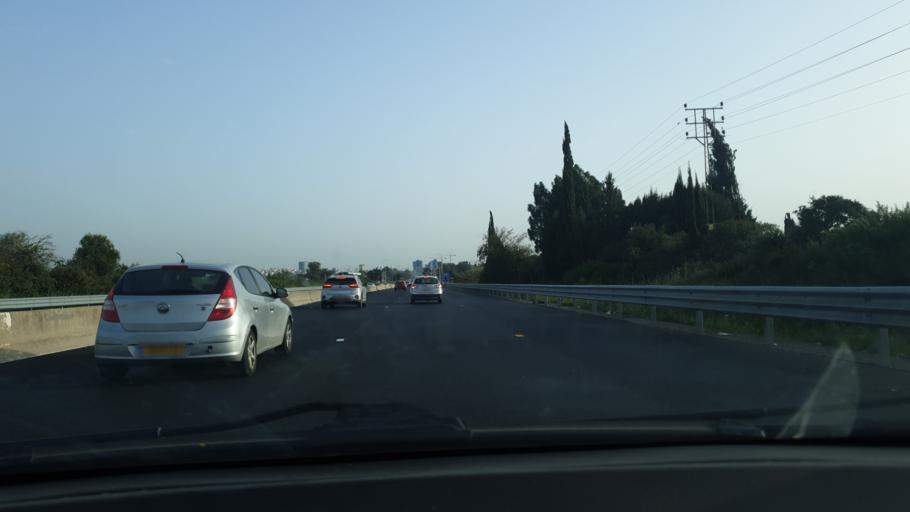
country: IL
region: Central District
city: Ra'anana
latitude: 32.2239
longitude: 34.8828
